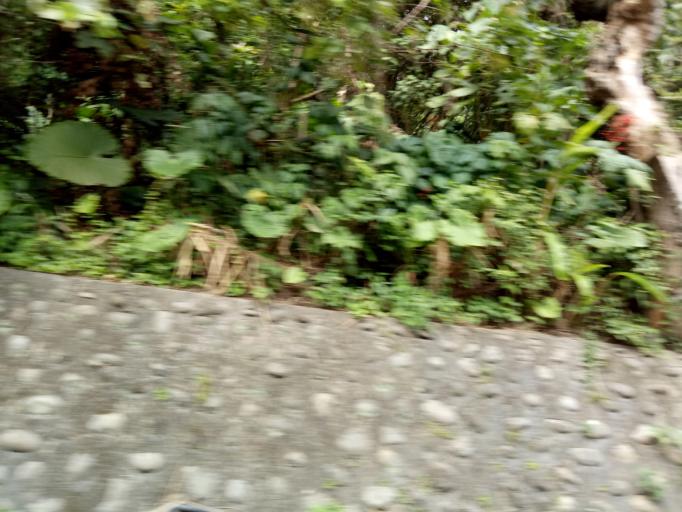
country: TW
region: Taiwan
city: Daxi
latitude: 24.8943
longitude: 121.2827
